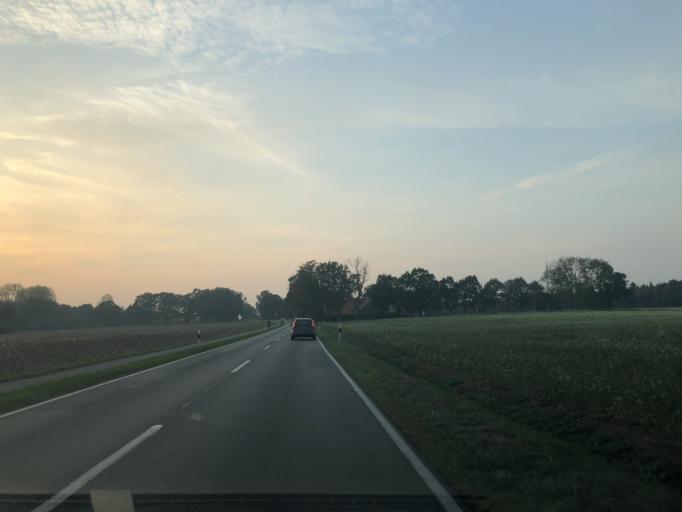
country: DE
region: Lower Saxony
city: Bosel
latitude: 53.0082
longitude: 7.9347
